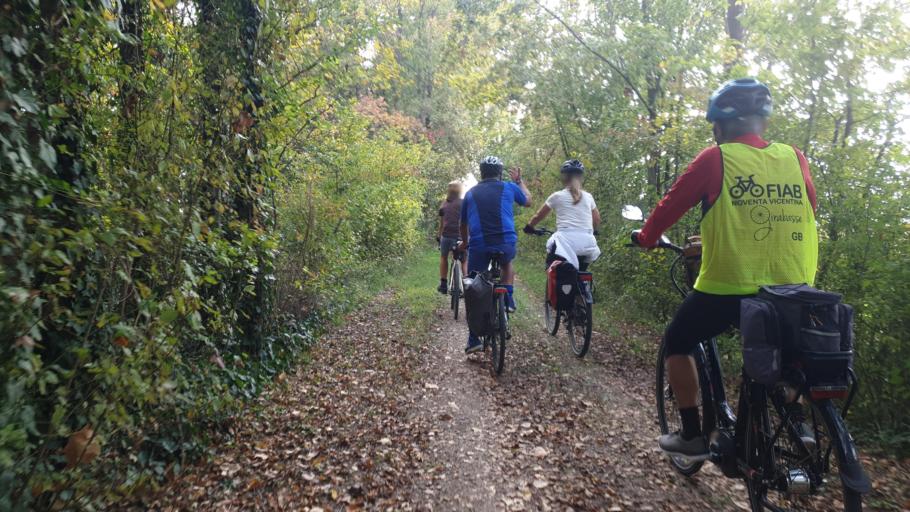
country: IT
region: Veneto
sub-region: Provincia di Vicenza
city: Poiana Maggiore
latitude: 45.2792
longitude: 11.4890
